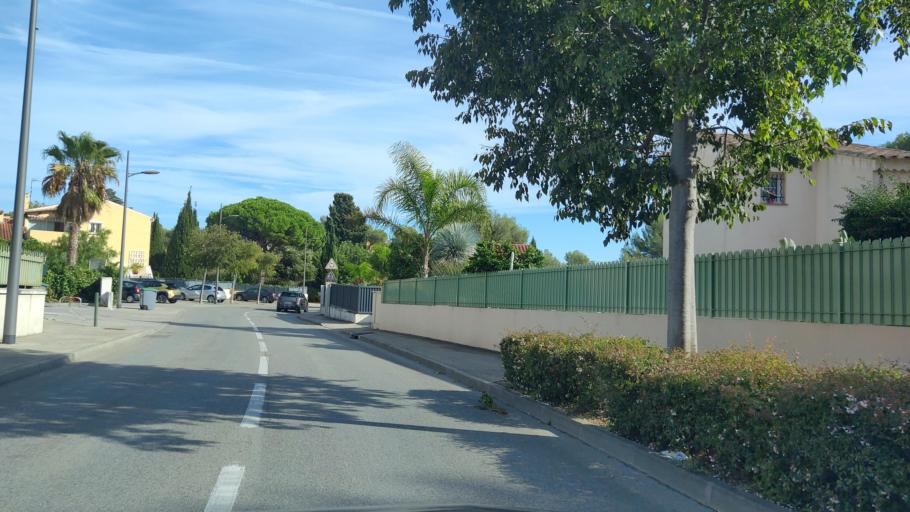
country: FR
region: Provence-Alpes-Cote d'Azur
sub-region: Departement du Var
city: Sanary-sur-Mer
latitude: 43.1245
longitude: 5.8019
